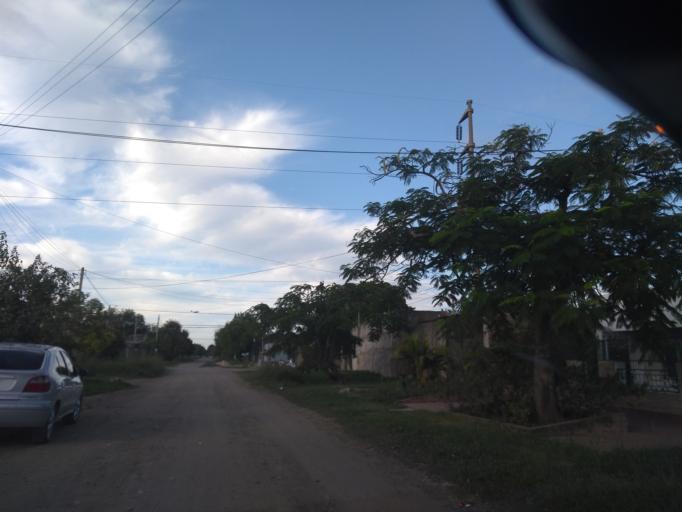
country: AR
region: Chaco
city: Barranqueras
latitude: -27.4903
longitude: -58.9373
